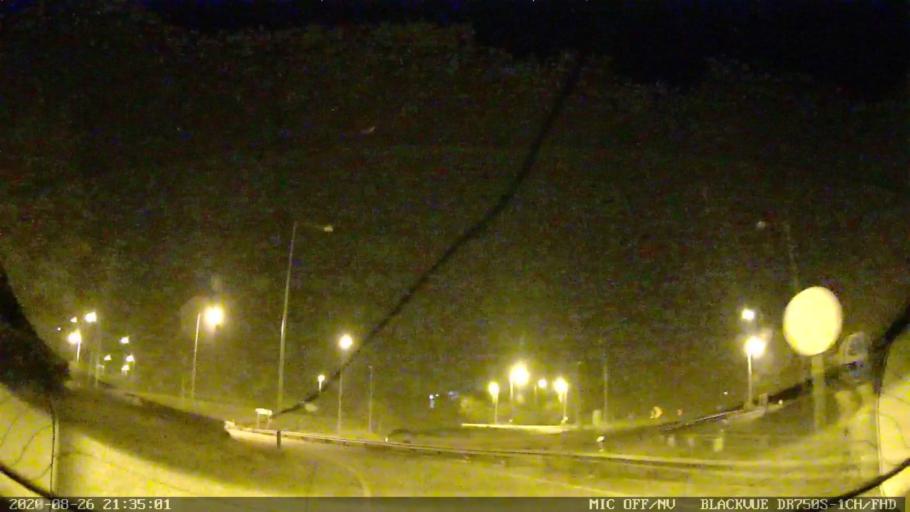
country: PT
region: Viseu
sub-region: Viseu
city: Rio de Loba
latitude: 40.6799
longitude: -7.8820
